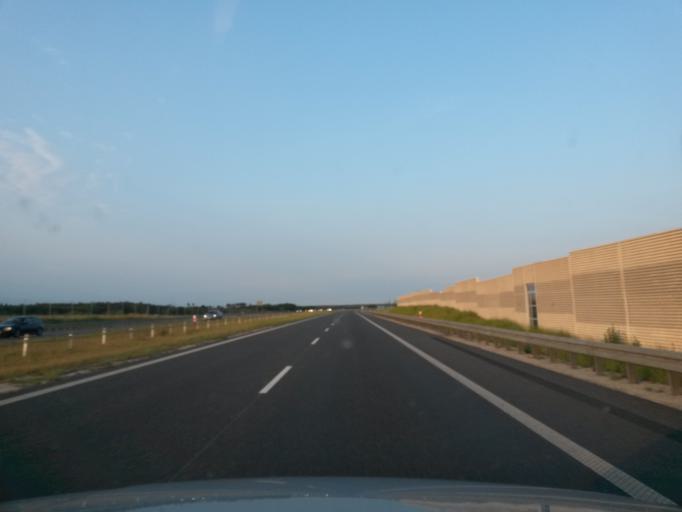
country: PL
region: Lodz Voivodeship
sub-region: Powiat wieruszowski
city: Sokolniki
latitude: 51.3226
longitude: 18.3137
